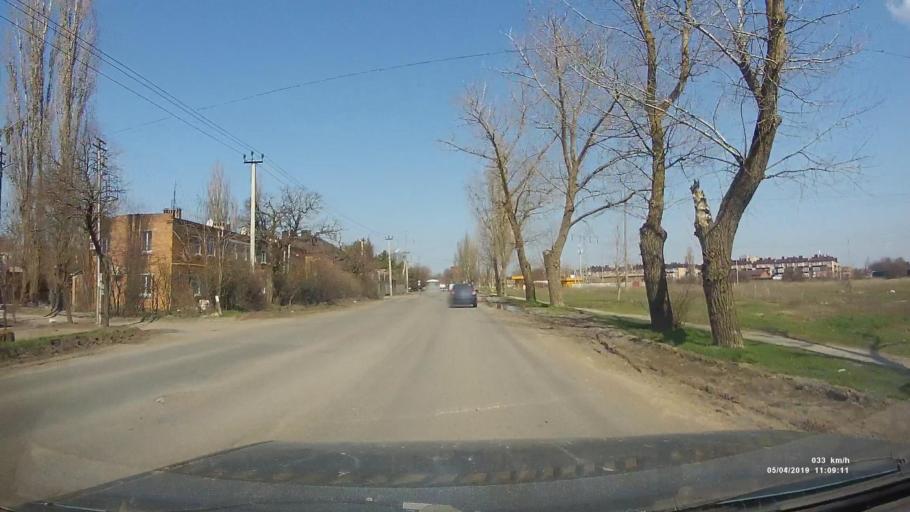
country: RU
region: Rostov
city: Azov
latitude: 47.0893
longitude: 39.4335
